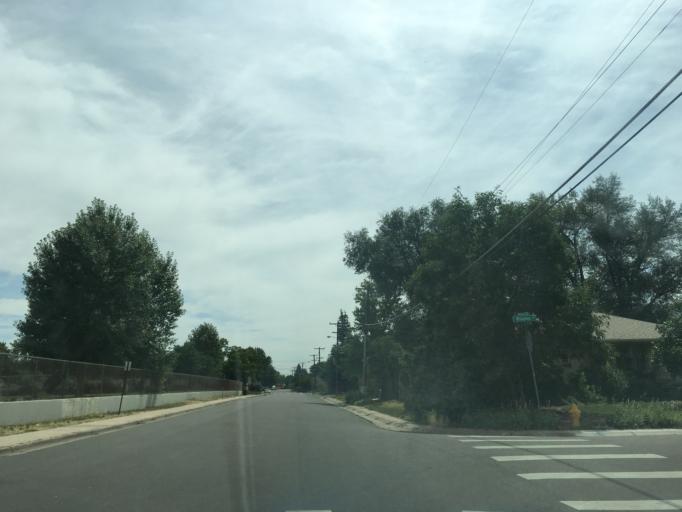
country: US
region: Colorado
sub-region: Jefferson County
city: Lakewood
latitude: 39.6882
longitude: -105.0473
